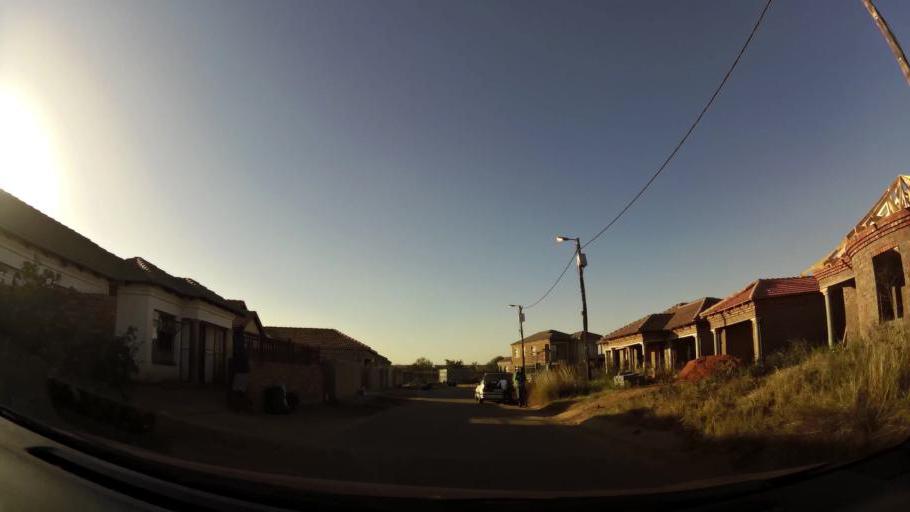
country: ZA
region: Gauteng
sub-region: City of Tshwane Metropolitan Municipality
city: Mabopane
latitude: -25.5931
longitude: 28.1072
